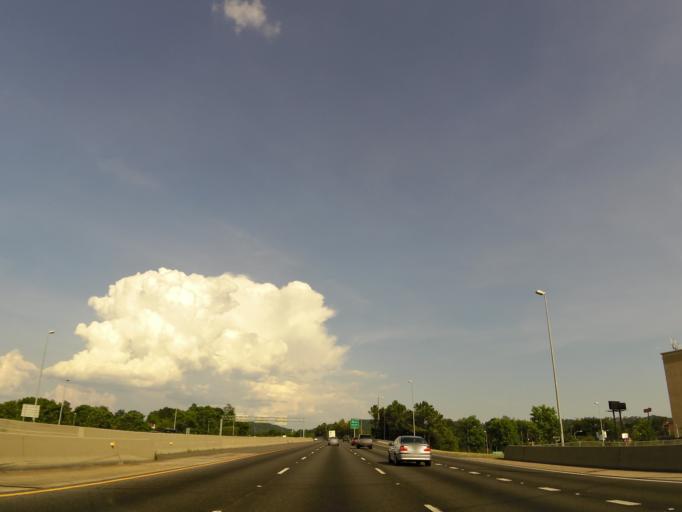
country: US
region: Alabama
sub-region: Jefferson County
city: Tarrant
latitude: 33.5456
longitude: -86.7615
